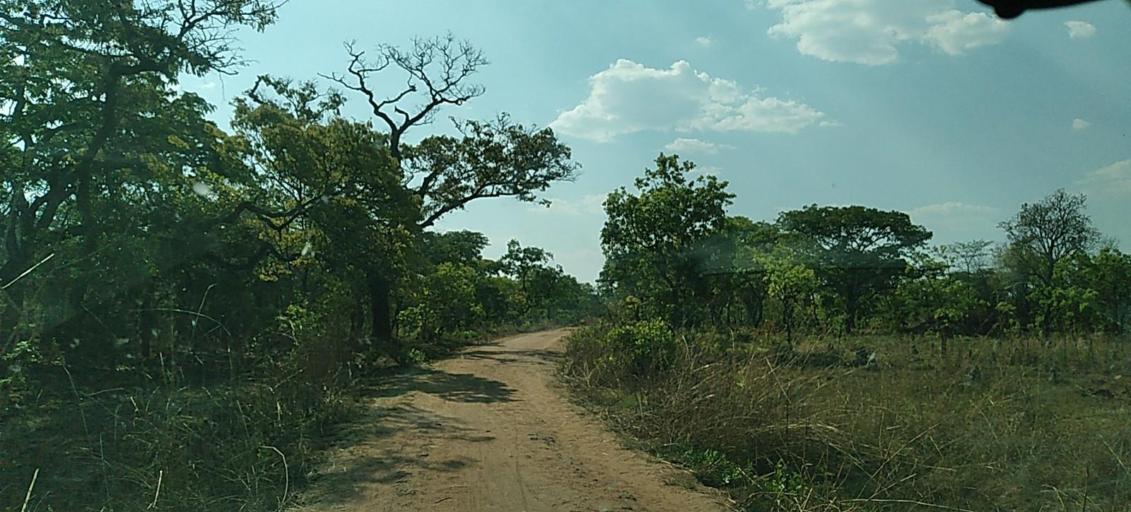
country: ZM
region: North-Western
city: Kalengwa
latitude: -13.1056
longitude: 24.9894
